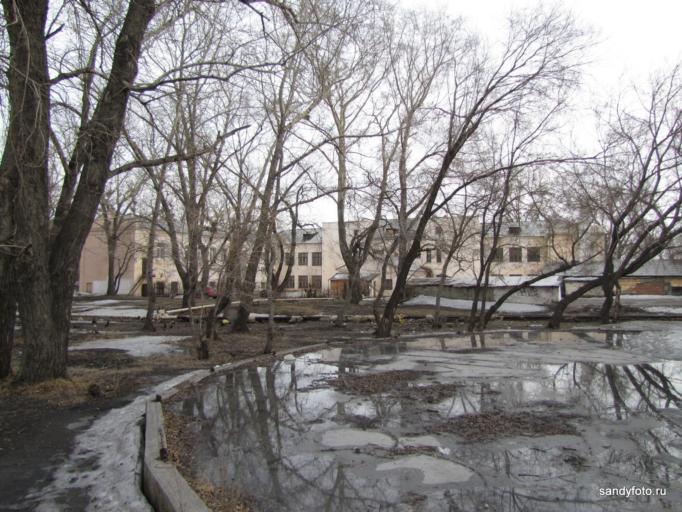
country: RU
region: Chelyabinsk
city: Troitsk
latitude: 54.1117
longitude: 61.5664
